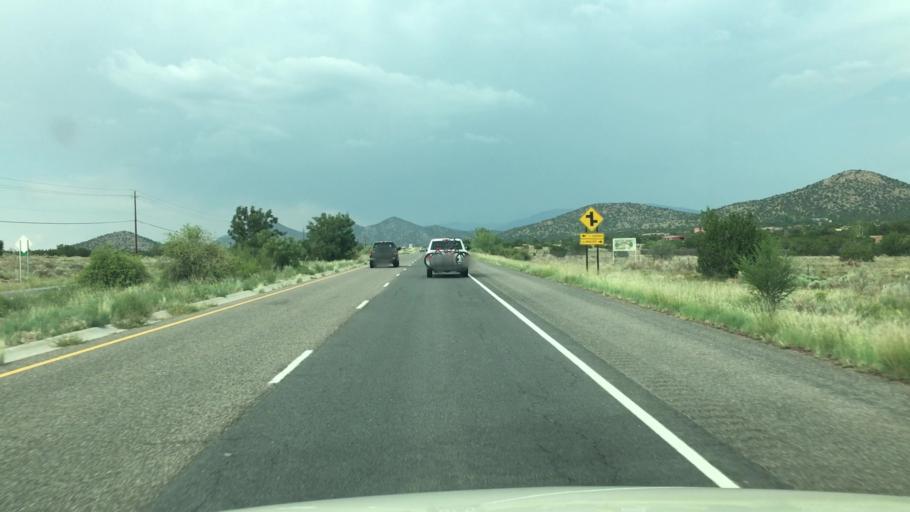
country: US
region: New Mexico
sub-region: Santa Fe County
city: Eldorado at Santa Fe
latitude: 35.5246
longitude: -105.8914
